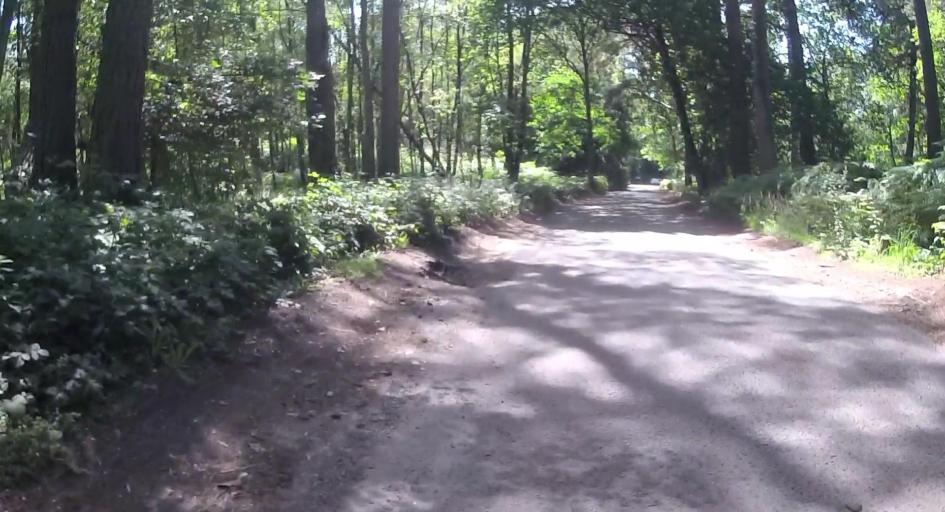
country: GB
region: England
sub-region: Surrey
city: Churt
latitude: 51.1682
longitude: -0.7798
